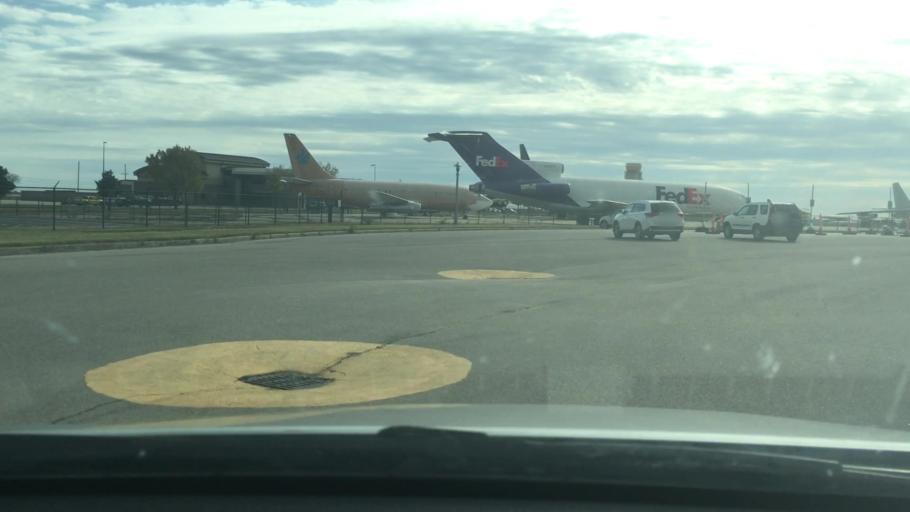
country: US
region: Kansas
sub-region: Sedgwick County
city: Derby
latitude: 37.6329
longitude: -97.2731
